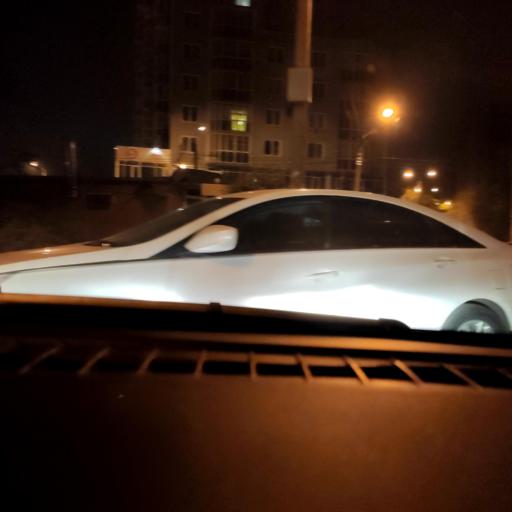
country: RU
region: Voronezj
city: Voronezh
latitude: 51.6419
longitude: 39.1445
